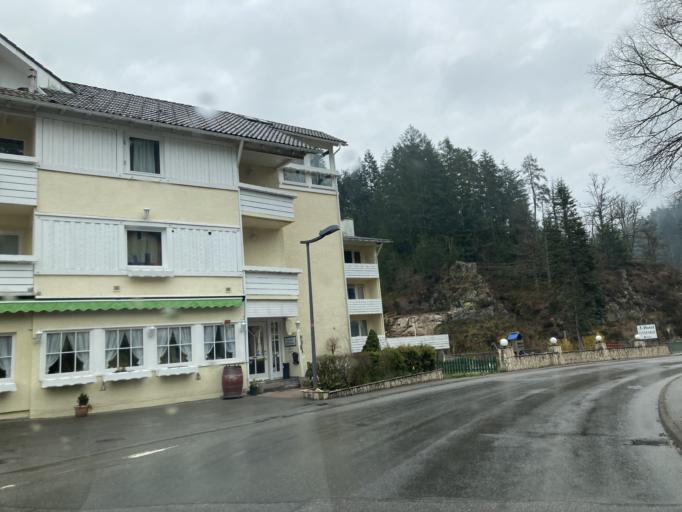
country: DE
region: Baden-Wuerttemberg
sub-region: Freiburg Region
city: Lauterbach/Schwarzwald
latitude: 48.2263
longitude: 8.3570
